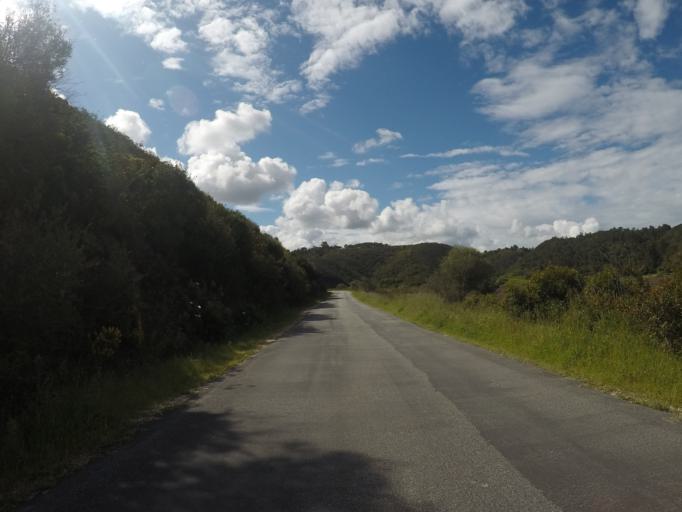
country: PT
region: Beja
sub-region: Odemira
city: Sao Teotonio
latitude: 37.4370
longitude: -8.7872
